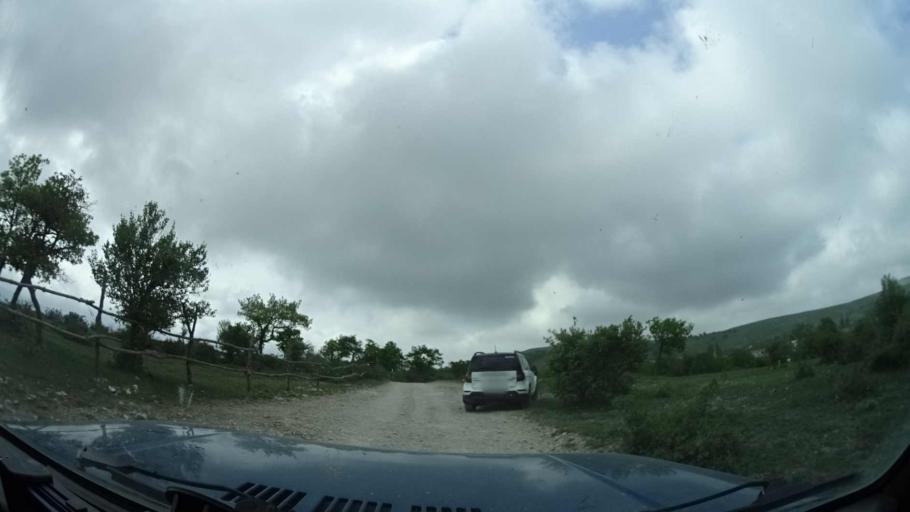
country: RU
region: Dagestan
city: Dubki
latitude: 43.0195
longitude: 46.8322
